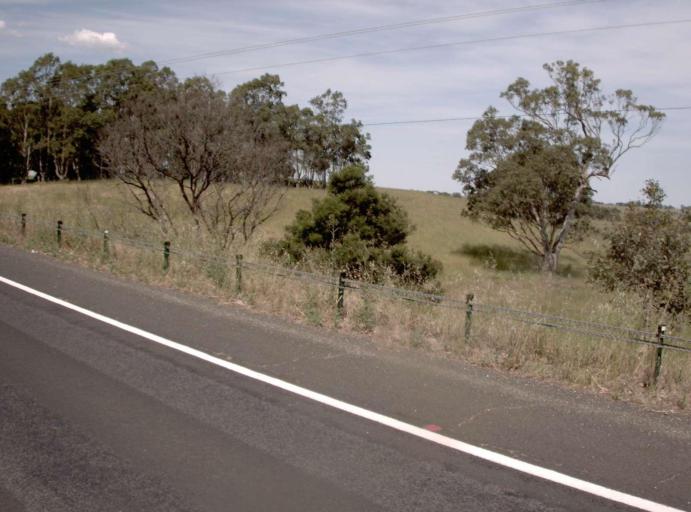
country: AU
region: Victoria
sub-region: East Gippsland
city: Bairnsdale
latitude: -37.8252
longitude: 147.7182
